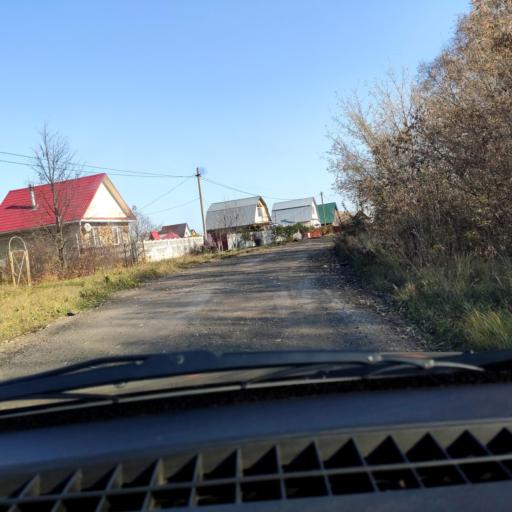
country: RU
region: Bashkortostan
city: Avdon
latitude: 54.4914
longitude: 55.8444
